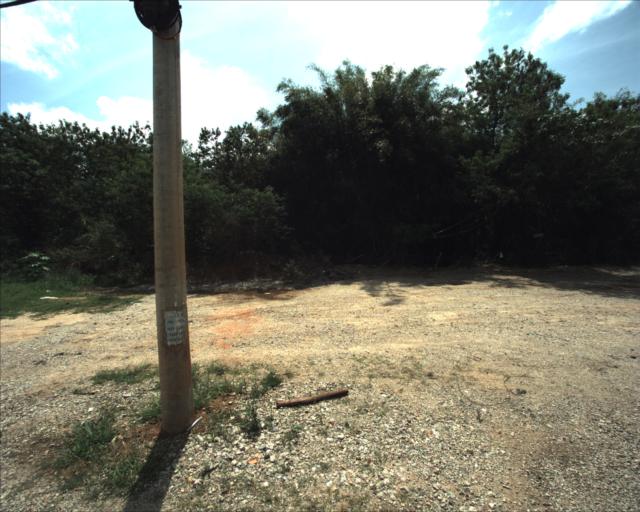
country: BR
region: Sao Paulo
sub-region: Sorocaba
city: Sorocaba
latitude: -23.4234
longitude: -47.4073
